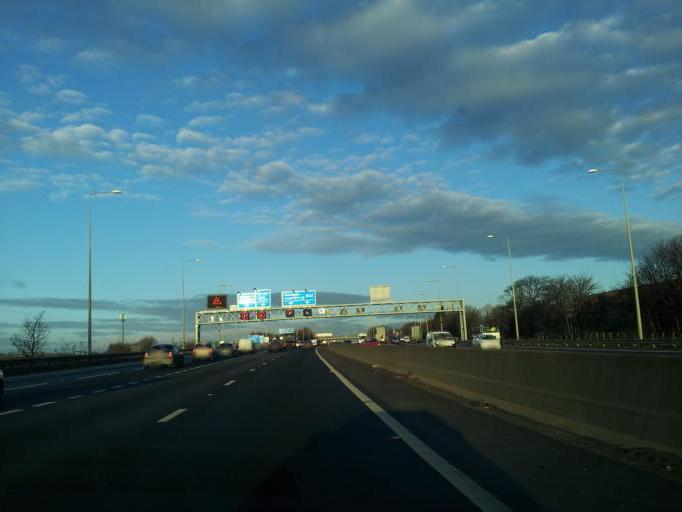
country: GB
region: England
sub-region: City and Borough of Leeds
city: Lofthouse
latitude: 53.7288
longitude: -1.5021
